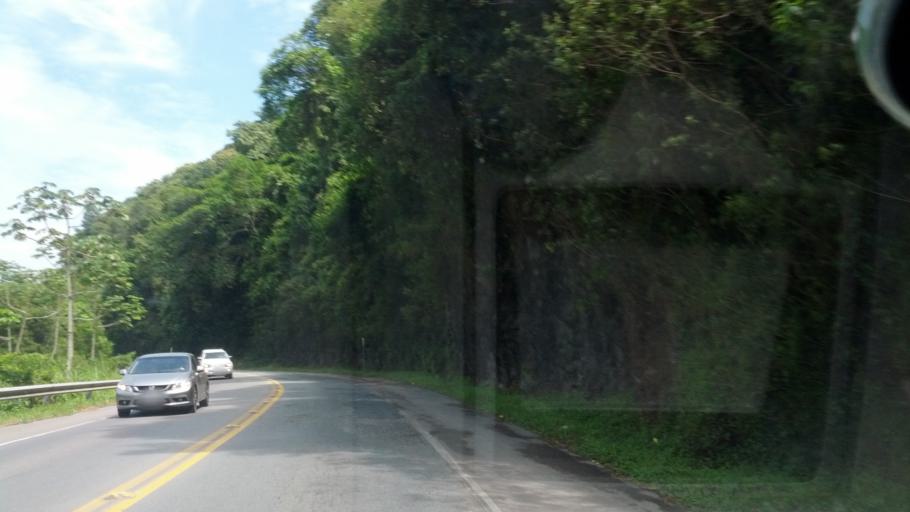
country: BR
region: Santa Catarina
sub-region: Ibirama
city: Ibirama
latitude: -27.0817
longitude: -49.5022
